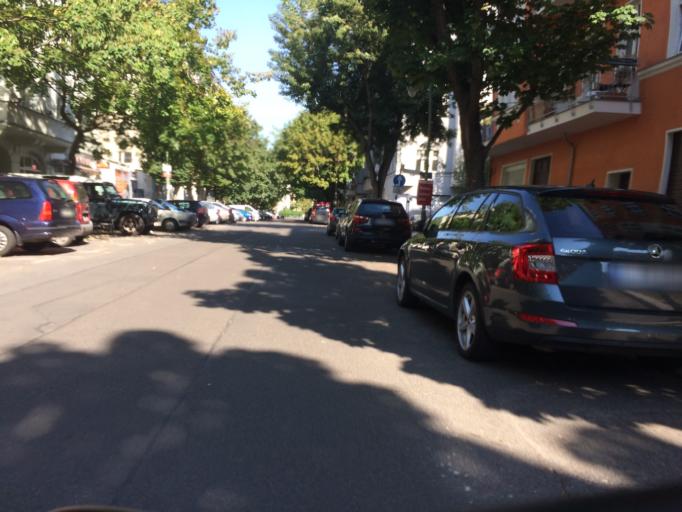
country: DE
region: Berlin
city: Prenzlauer Berg Bezirk
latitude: 52.5425
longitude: 13.4233
